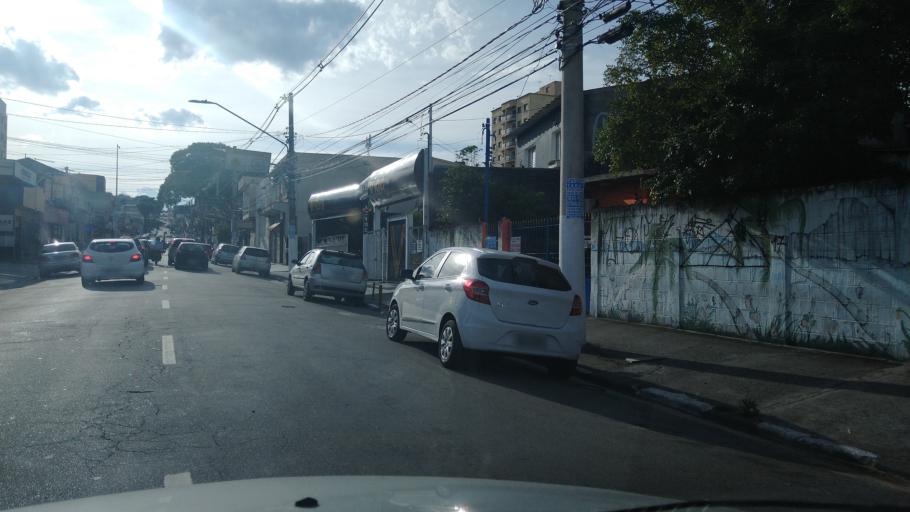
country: BR
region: Sao Paulo
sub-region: Osasco
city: Osasco
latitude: -23.5314
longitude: -46.7985
